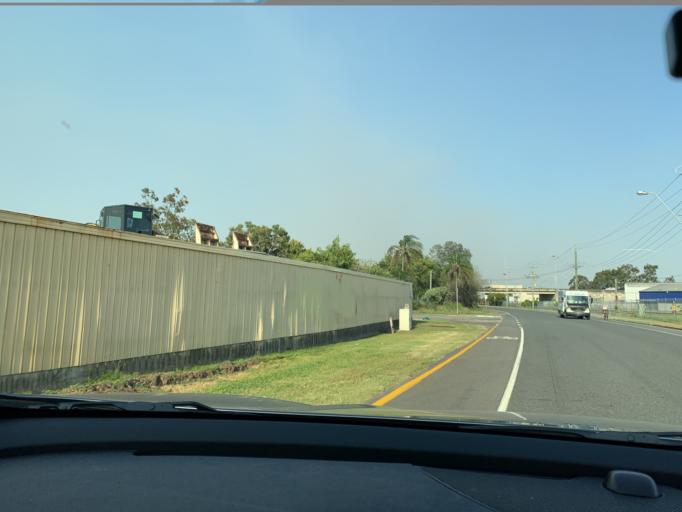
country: AU
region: Queensland
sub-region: Brisbane
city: Ascot
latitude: -27.4314
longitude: 153.0790
